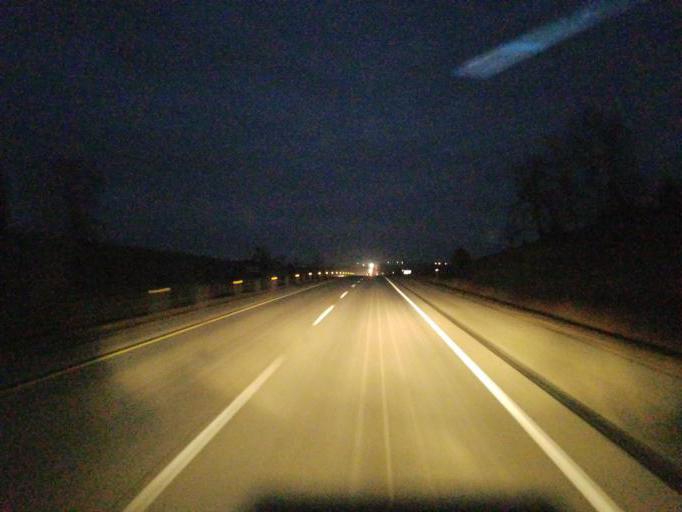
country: US
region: Iowa
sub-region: Guthrie County
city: Stuart
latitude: 41.4960
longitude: -94.4950
